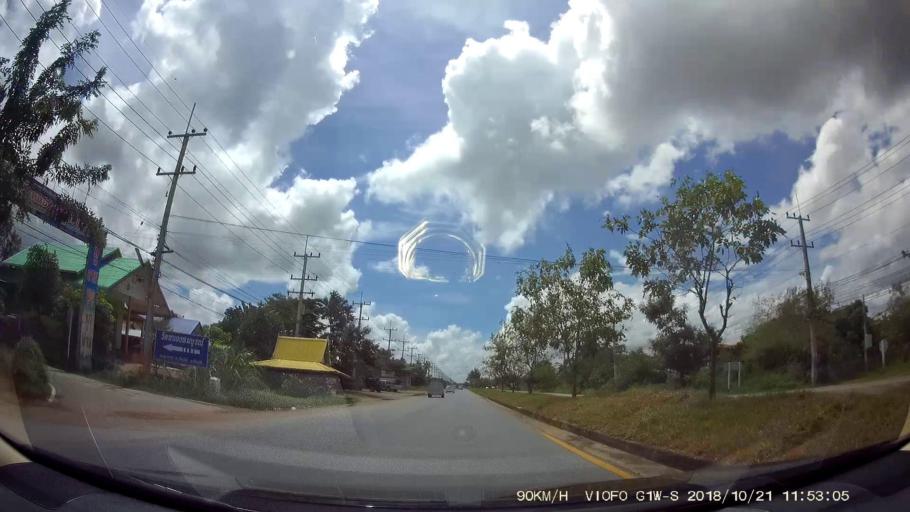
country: TH
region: Chaiyaphum
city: Chatturat
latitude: 15.6004
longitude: 101.9079
